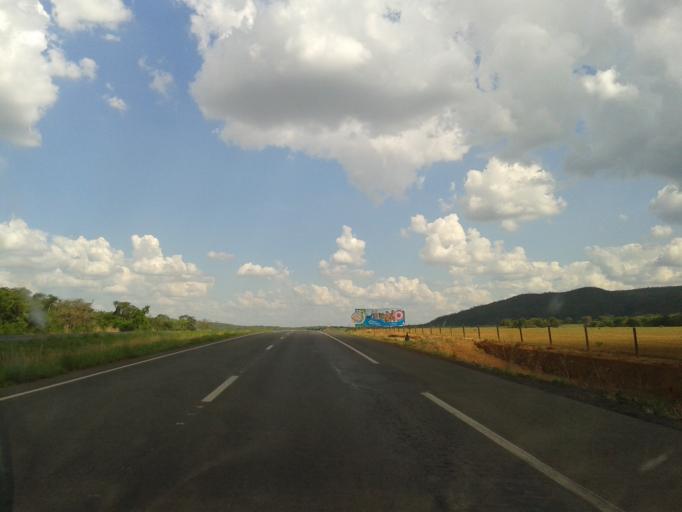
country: BR
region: Goias
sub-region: Caldas Novas
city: Caldas Novas
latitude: -17.7125
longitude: -48.6970
